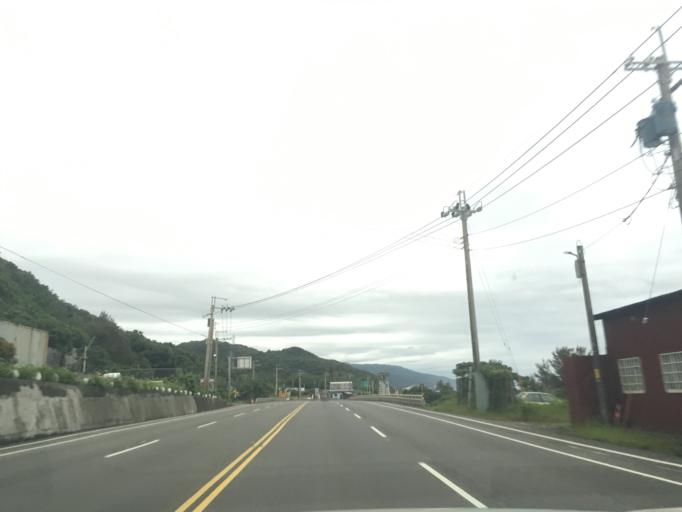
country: TW
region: Taiwan
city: Hengchun
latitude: 22.3014
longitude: 120.8888
